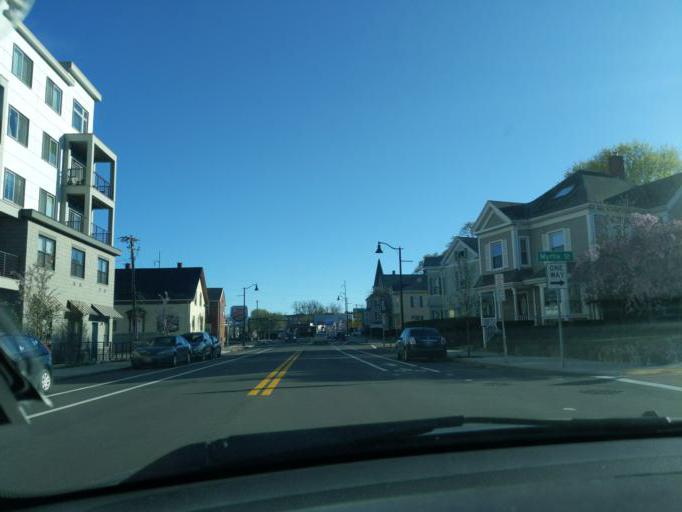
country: US
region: Massachusetts
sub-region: Essex County
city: Beverly
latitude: 42.5562
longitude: -70.8807
